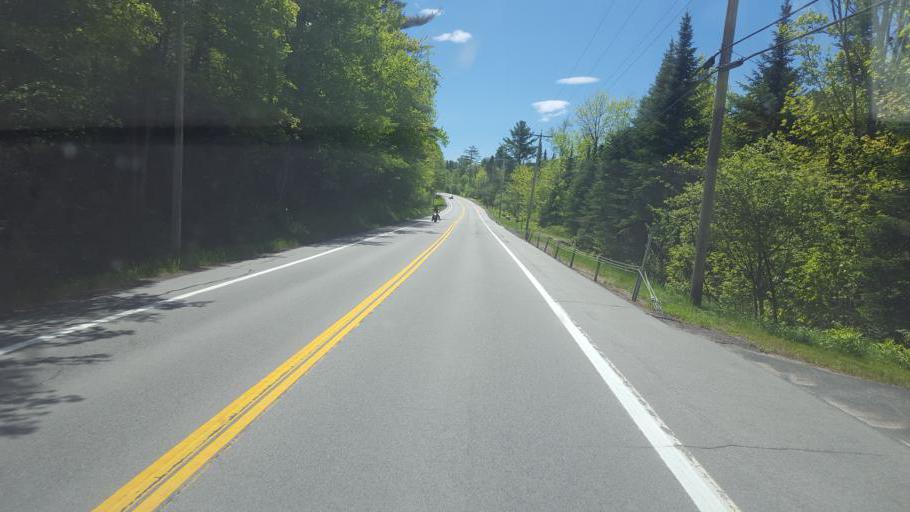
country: US
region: New York
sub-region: Hamilton County
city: Lake Pleasant
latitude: 43.4404
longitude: -74.4780
